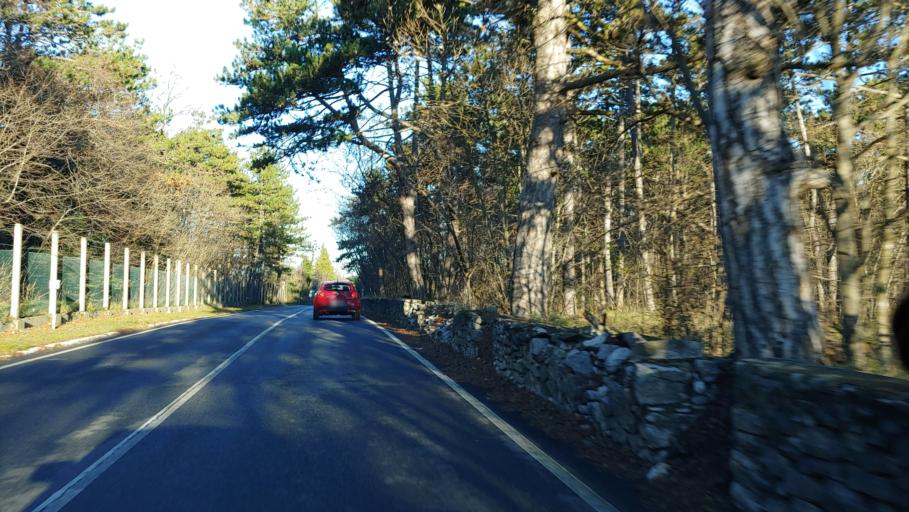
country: IT
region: Friuli Venezia Giulia
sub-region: Provincia di Trieste
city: Trieste
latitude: 45.6653
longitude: 13.8322
